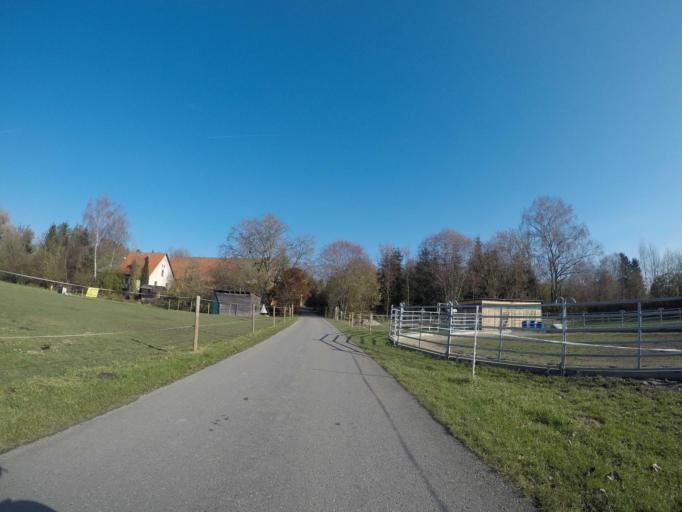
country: DE
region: Baden-Wuerttemberg
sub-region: Tuebingen Region
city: Riedlingen
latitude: 48.1595
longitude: 9.4924
